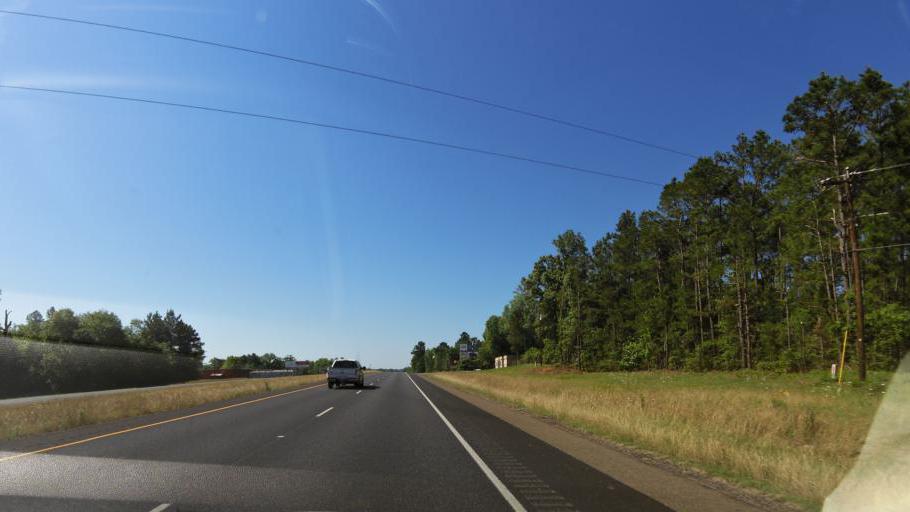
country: US
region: Texas
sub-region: Angelina County
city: Redland
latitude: 31.4675
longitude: -94.7266
